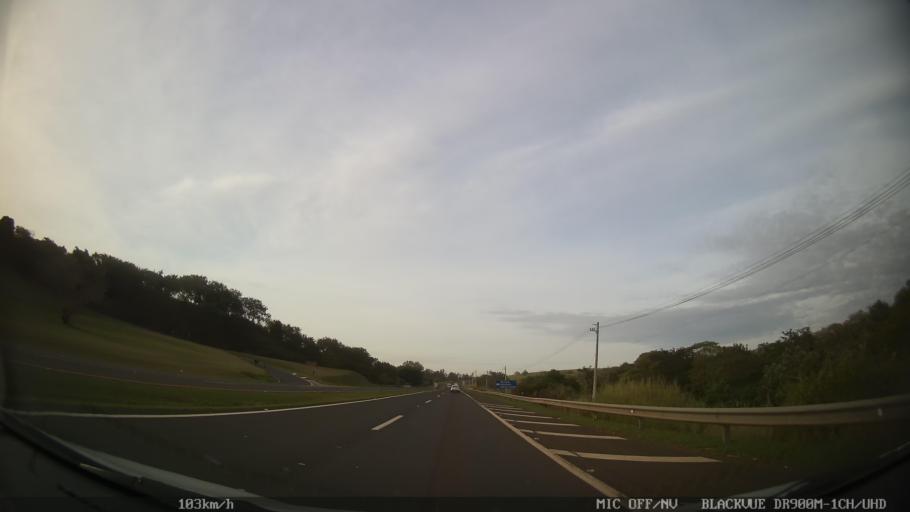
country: BR
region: Sao Paulo
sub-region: Piracicaba
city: Piracicaba
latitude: -22.6856
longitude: -47.5812
